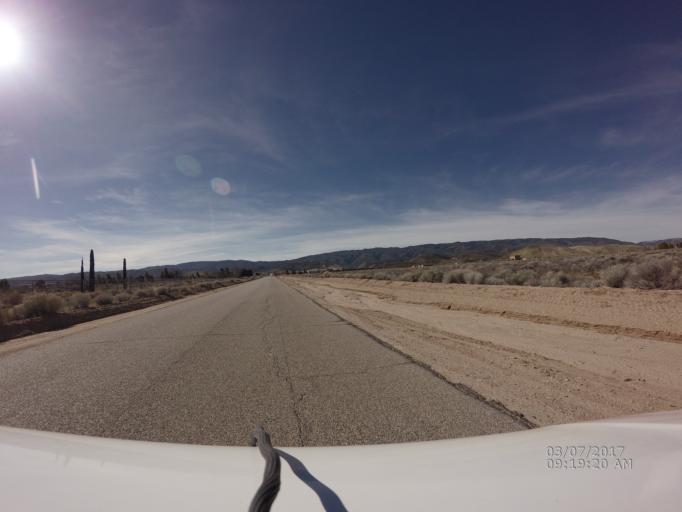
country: US
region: California
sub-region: Los Angeles County
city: Green Valley
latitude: 34.7815
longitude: -118.5898
